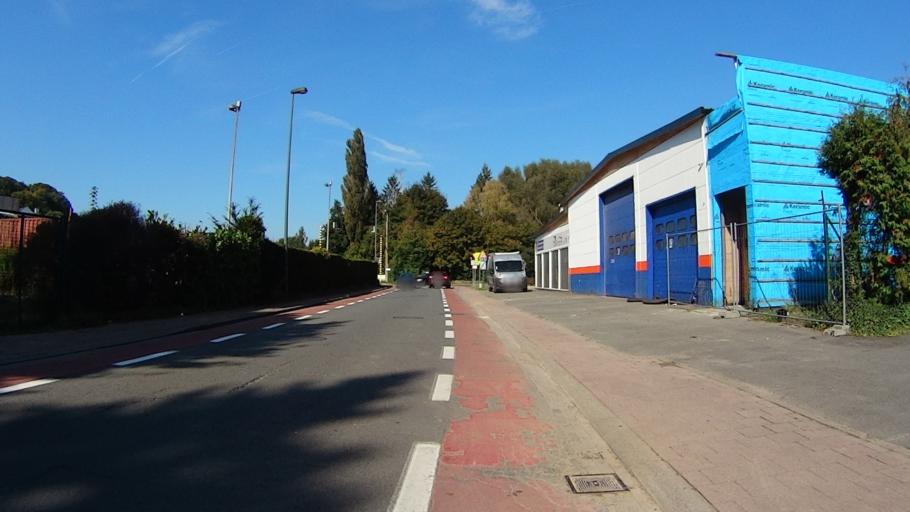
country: BE
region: Flanders
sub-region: Provincie Vlaams-Brabant
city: Hoeilaart
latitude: 50.7685
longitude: 4.4870
